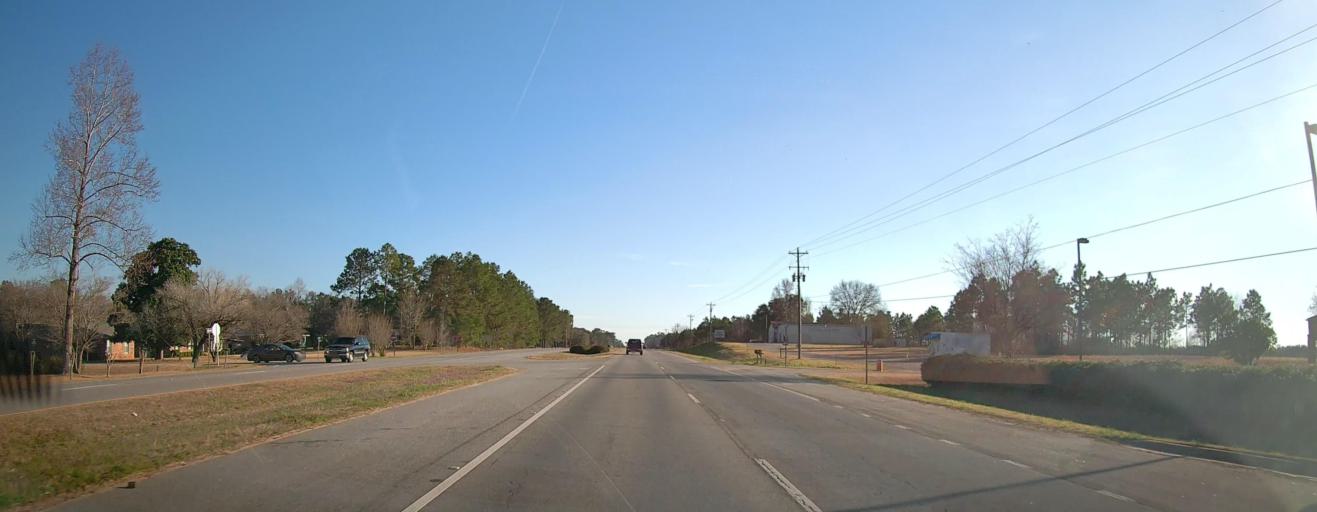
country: US
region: Georgia
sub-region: Lee County
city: Leesburg
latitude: 31.7158
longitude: -84.1725
